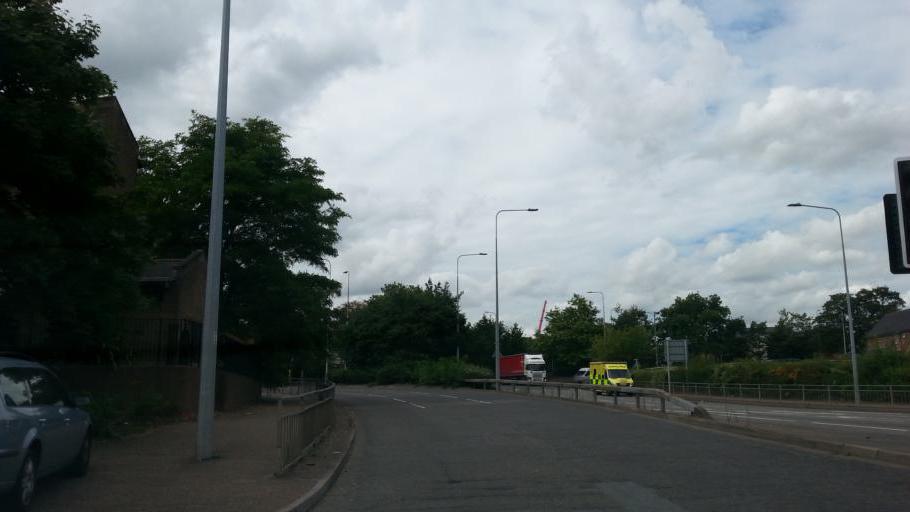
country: GB
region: England
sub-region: Essex
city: Chelmsford
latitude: 51.7406
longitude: 0.4686
